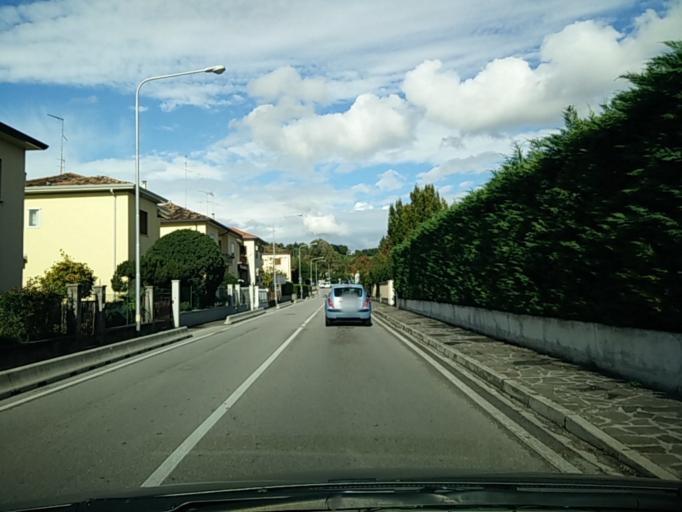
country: IT
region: Veneto
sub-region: Provincia di Treviso
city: Conegliano
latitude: 45.8769
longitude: 12.2812
